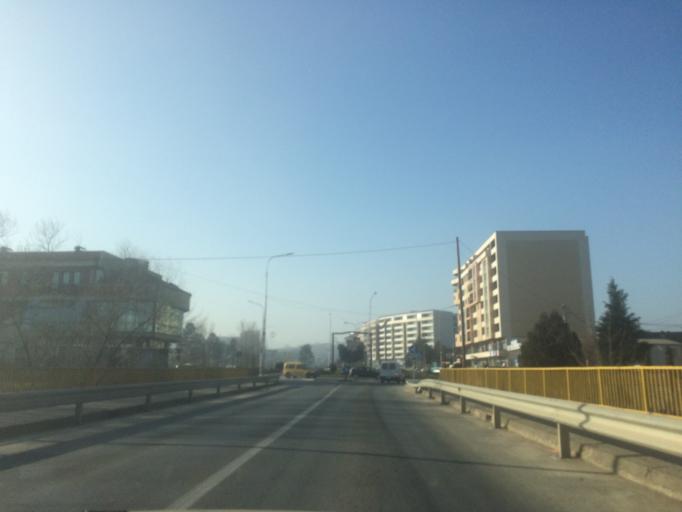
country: XK
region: Gjakova
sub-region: Komuna e Gjakoves
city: Gjakove
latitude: 42.3883
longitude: 20.4355
